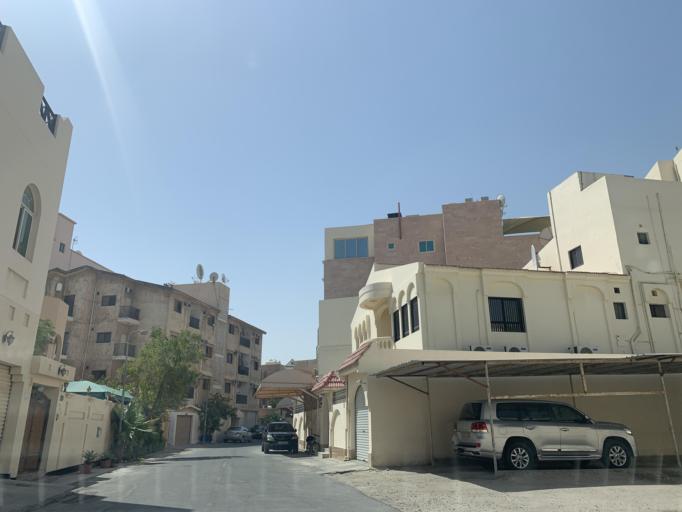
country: BH
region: Manama
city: Manama
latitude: 26.2069
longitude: 50.5827
